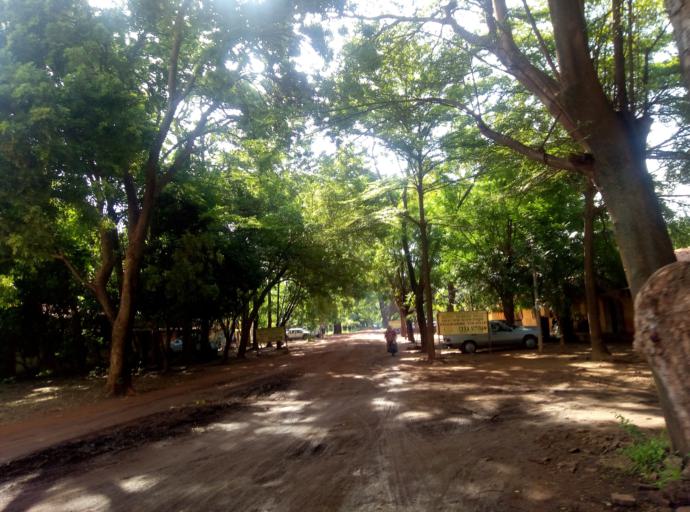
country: ML
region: Bamako
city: Bamako
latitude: 12.6539
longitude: -7.9285
